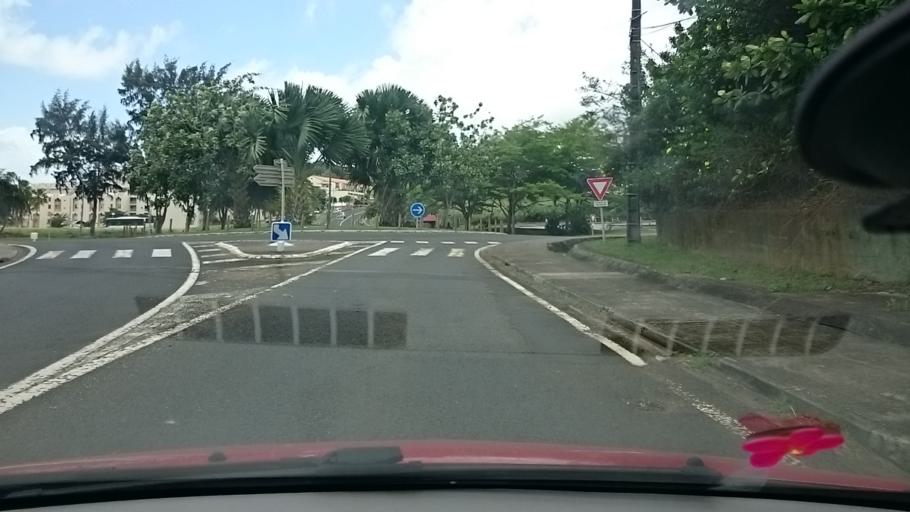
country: MQ
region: Martinique
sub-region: Martinique
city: La Trinite
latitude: 14.7468
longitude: -60.9465
